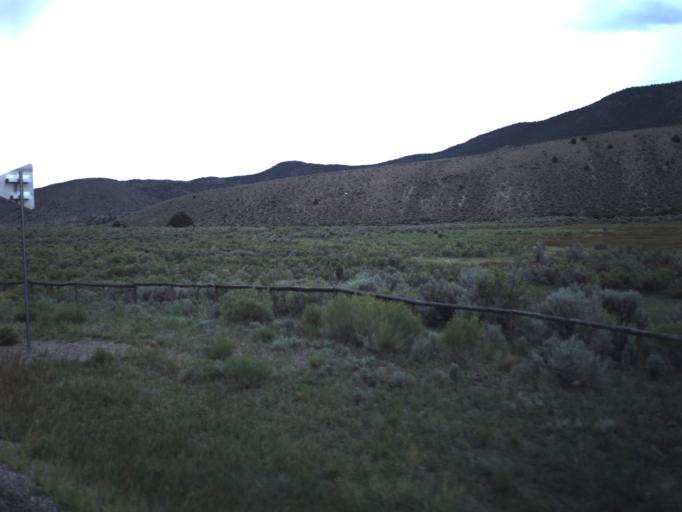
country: US
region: Utah
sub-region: Piute County
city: Junction
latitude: 38.1776
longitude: -112.0715
